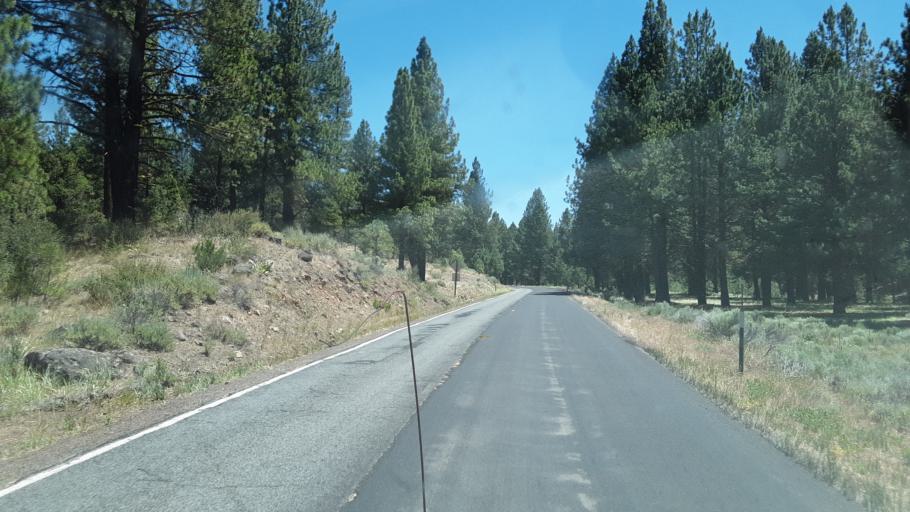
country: US
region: California
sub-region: Modoc County
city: Alturas
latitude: 41.0128
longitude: -120.8220
